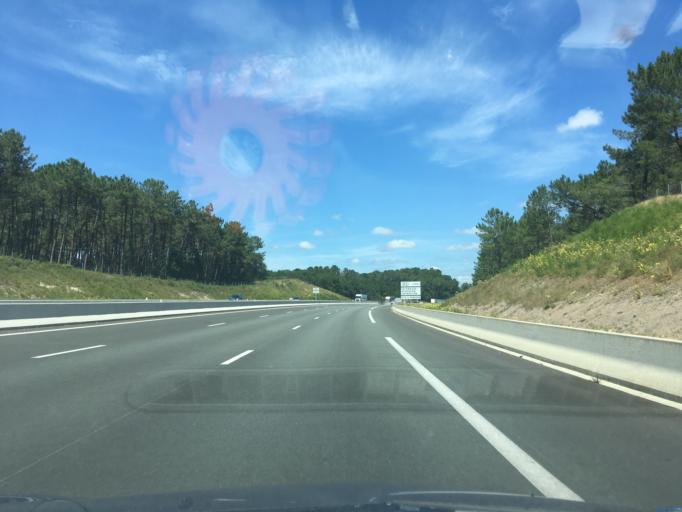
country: FR
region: Aquitaine
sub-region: Departement des Landes
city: Labenne
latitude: 43.6133
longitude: -1.4131
